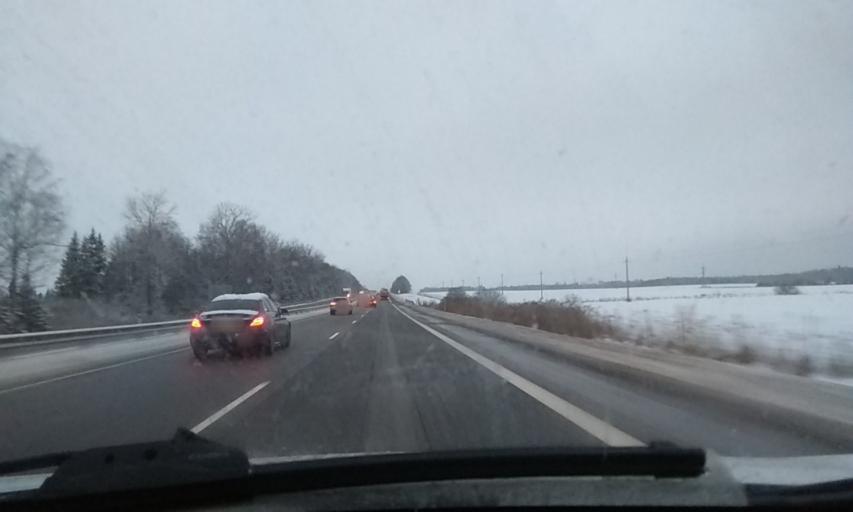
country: LT
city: Ziezmariai
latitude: 54.8226
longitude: 24.4111
